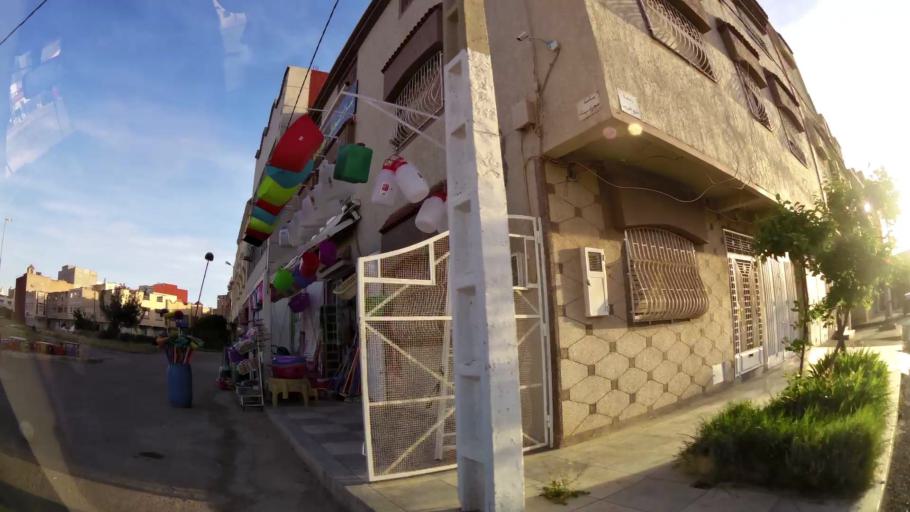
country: MA
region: Oriental
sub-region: Oujda-Angad
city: Oujda
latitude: 34.6791
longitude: -1.8897
